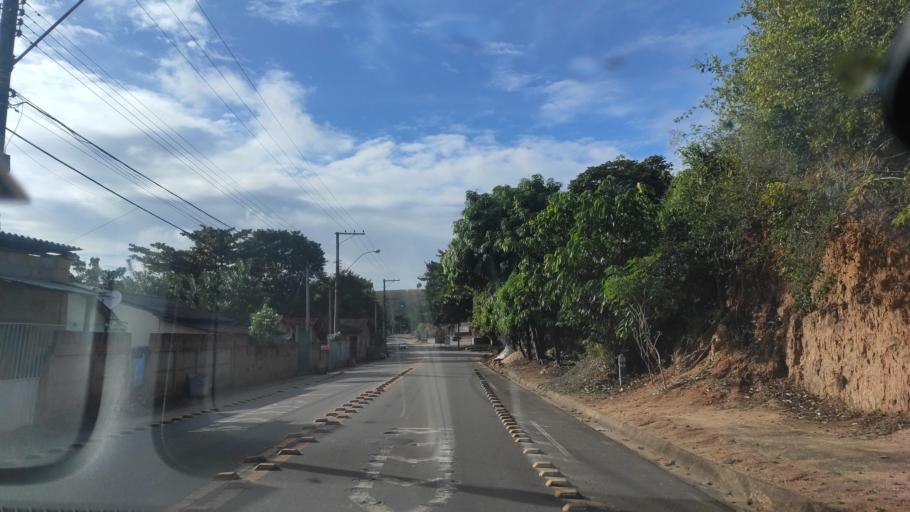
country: BR
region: Espirito Santo
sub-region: Nova Venecia
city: Nova Venecia
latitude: -18.7122
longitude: -40.3825
